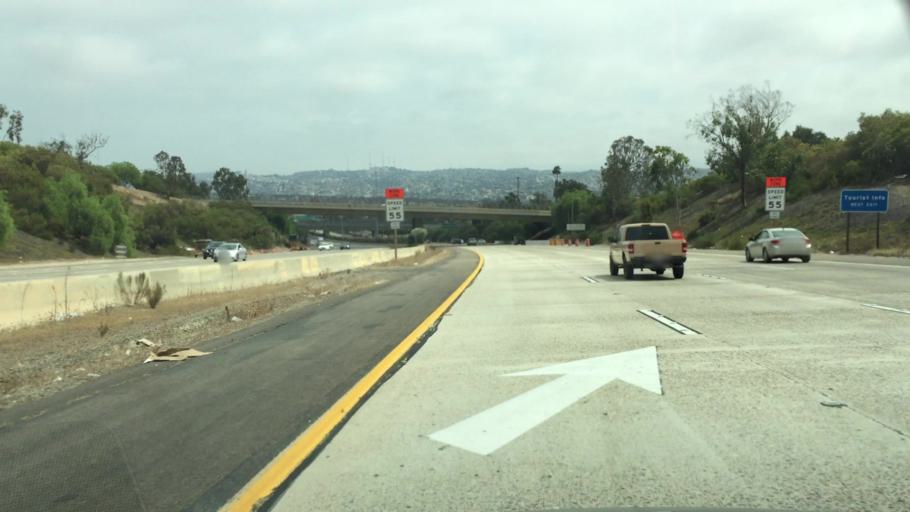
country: MX
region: Baja California
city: Tijuana
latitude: 32.5603
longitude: -117.0425
